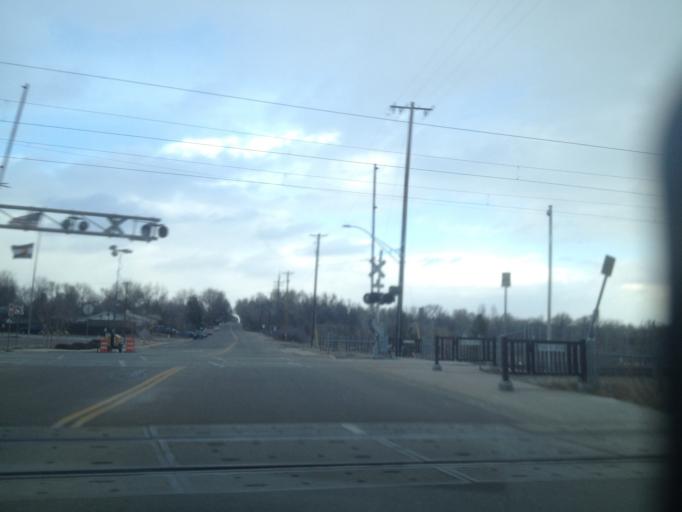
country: US
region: Colorado
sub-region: Adams County
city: Berkley
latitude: 39.8045
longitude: -105.0441
